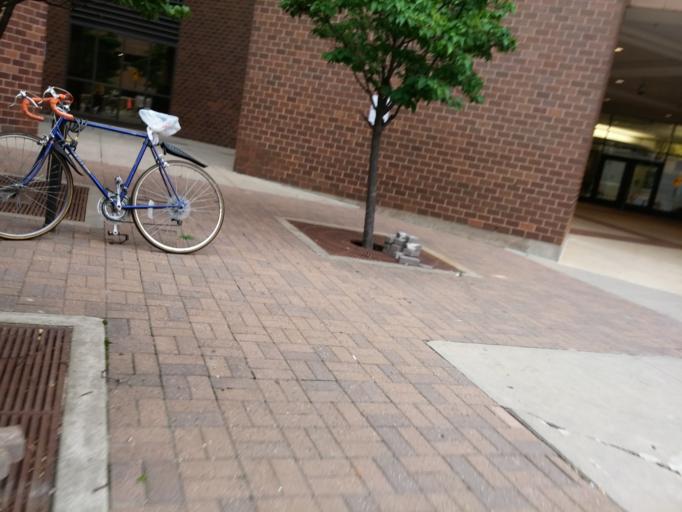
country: US
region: Wisconsin
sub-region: Dane County
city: Shorewood Hills
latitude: 43.0759
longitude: -89.4311
